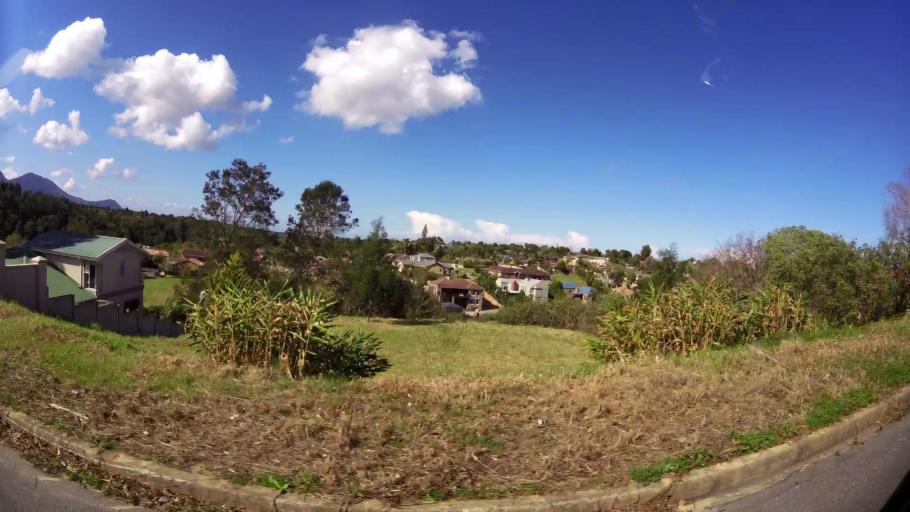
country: ZA
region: Western Cape
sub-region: Eden District Municipality
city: George
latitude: -33.9543
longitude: 22.4824
